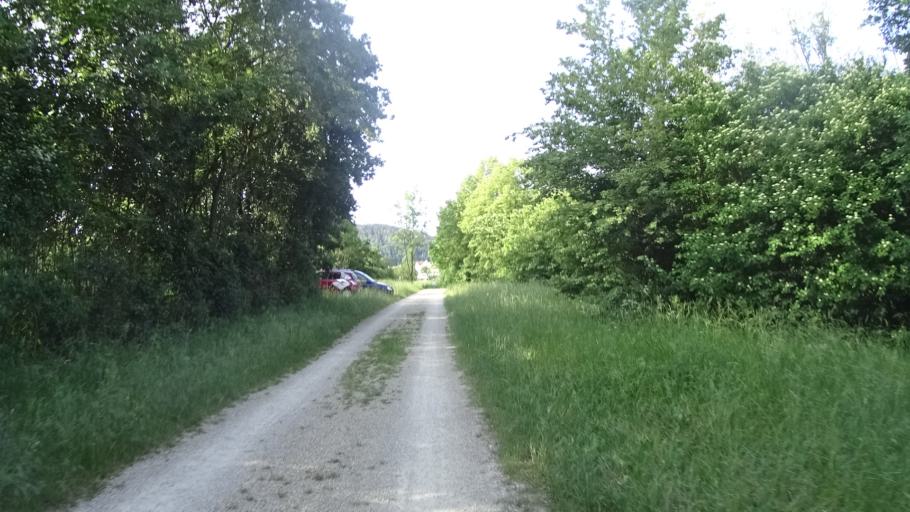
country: DE
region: Bavaria
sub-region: Lower Bavaria
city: Riedenburg
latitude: 48.9675
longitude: 11.6832
